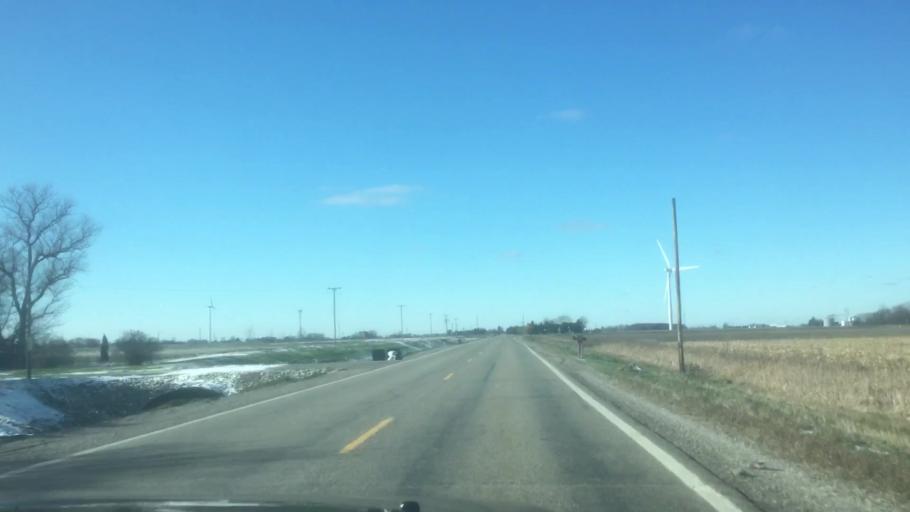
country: US
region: Michigan
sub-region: Tuscola County
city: Reese
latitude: 43.5227
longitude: -83.6555
